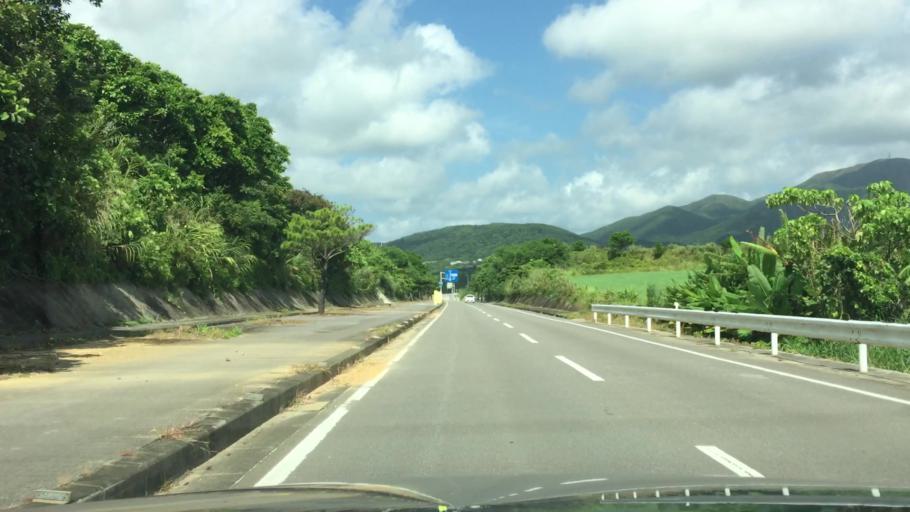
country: JP
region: Okinawa
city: Ishigaki
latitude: 24.4104
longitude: 124.2191
